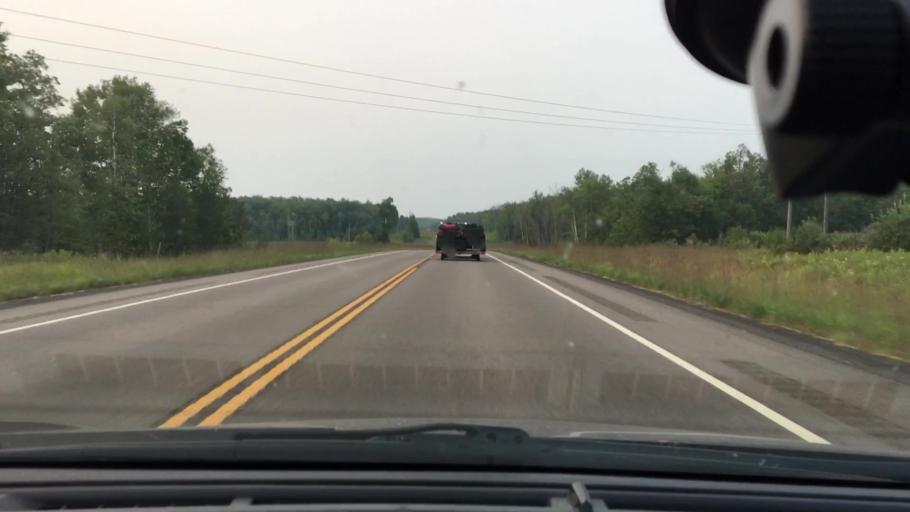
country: US
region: Minnesota
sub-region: Crow Wing County
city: Crosby
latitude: 46.6031
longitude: -93.9516
